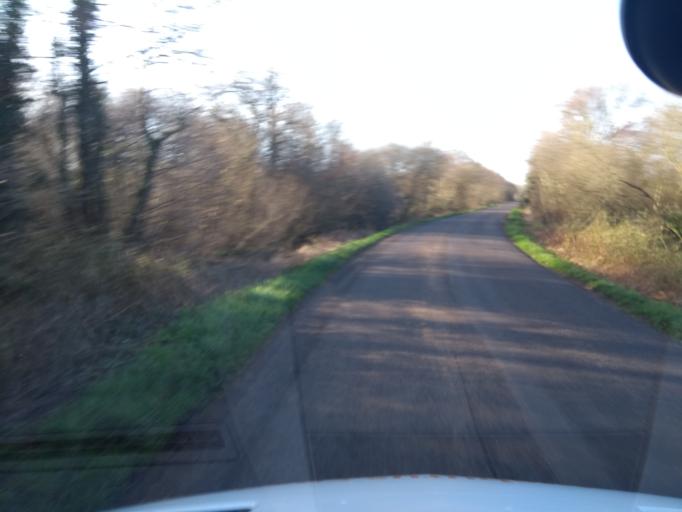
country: GB
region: England
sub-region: Somerset
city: Wedmore
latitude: 51.1655
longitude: -2.8267
